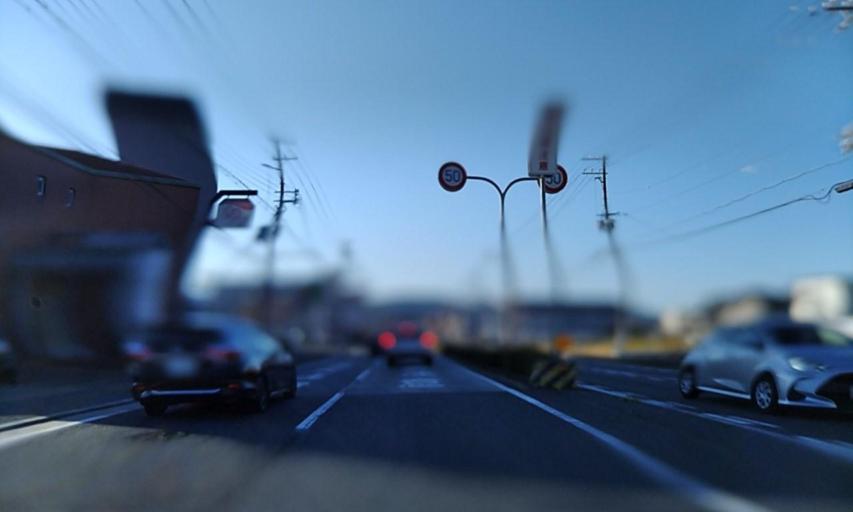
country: JP
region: Wakayama
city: Kainan
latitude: 34.1796
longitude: 135.1863
